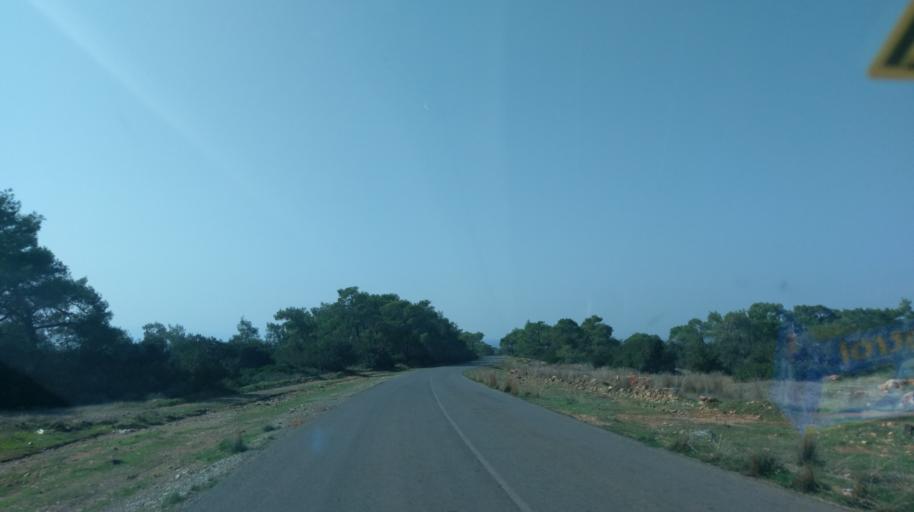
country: CY
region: Lefkosia
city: Morfou
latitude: 35.3012
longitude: 32.9900
